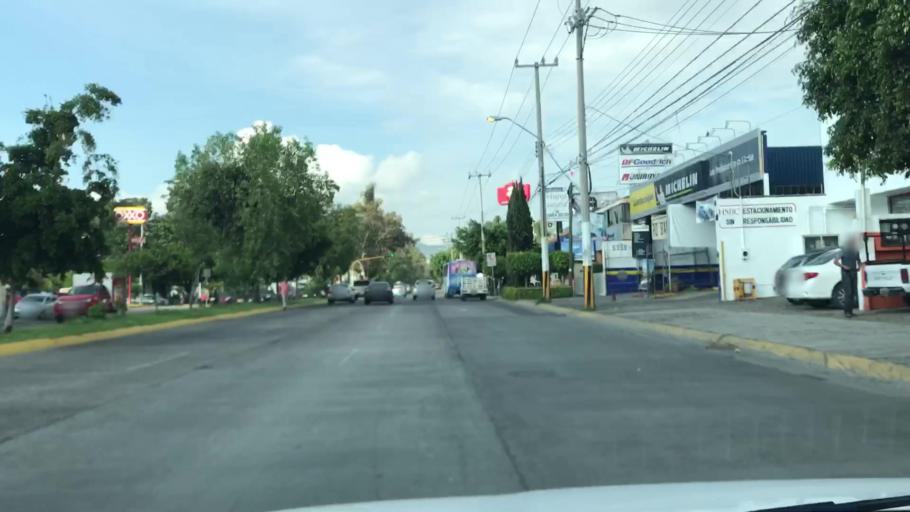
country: MX
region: Jalisco
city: Guadalajara
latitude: 20.6347
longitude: -103.4251
